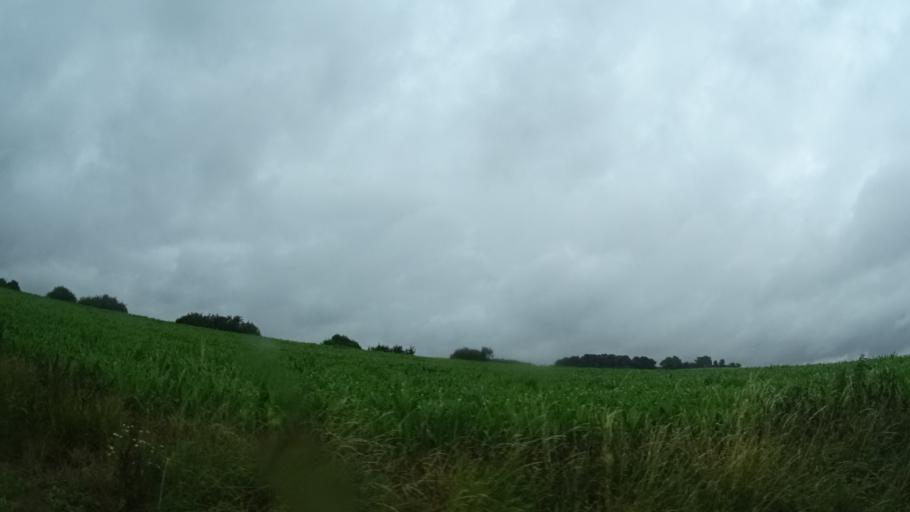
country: LU
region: Luxembourg
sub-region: Canton de Capellen
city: Clemency
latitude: 49.5947
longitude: 5.8537
